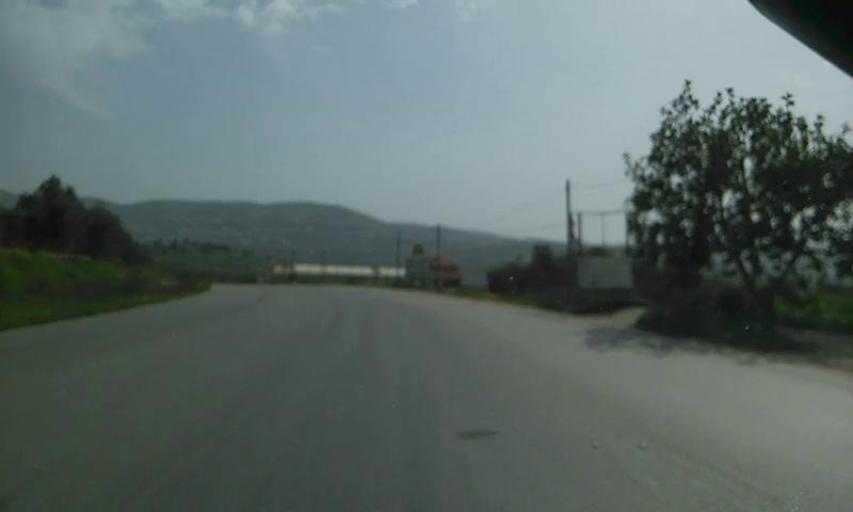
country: PS
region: West Bank
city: `Ajjah
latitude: 32.3470
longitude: 35.2010
